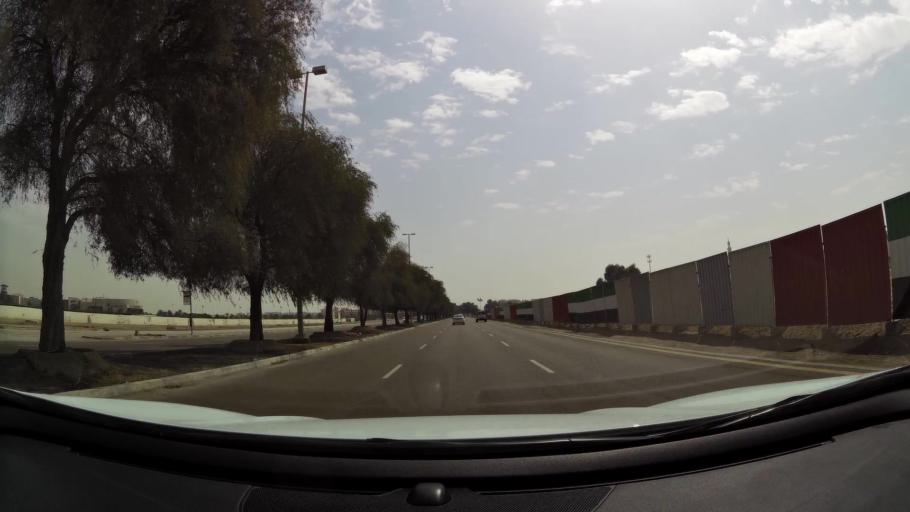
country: AE
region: Abu Dhabi
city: Abu Dhabi
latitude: 24.3100
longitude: 54.6147
